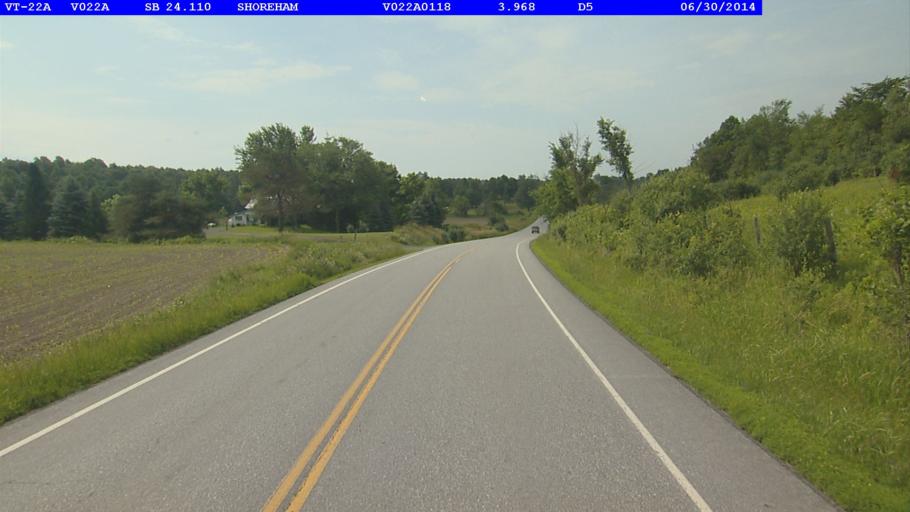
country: US
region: New York
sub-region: Essex County
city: Ticonderoga
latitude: 43.9068
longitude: -73.3085
